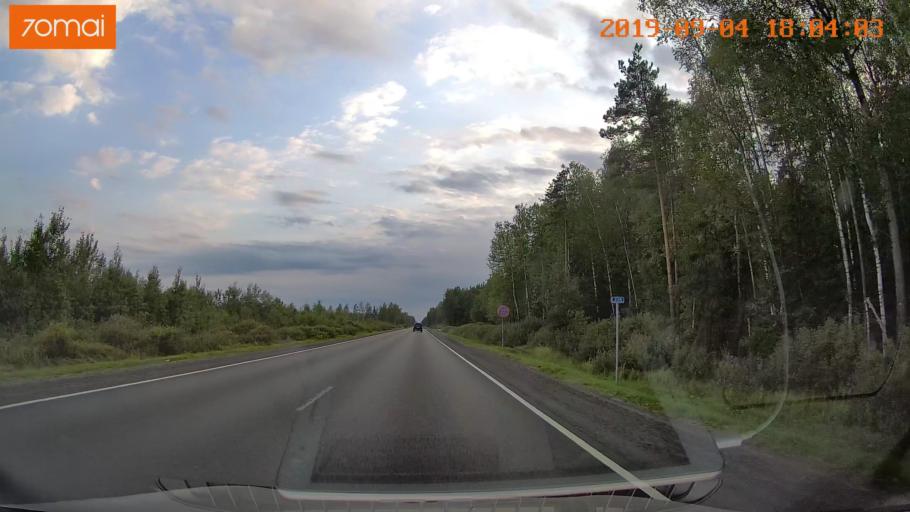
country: RU
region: Moskovskaya
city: Il'inskiy Pogost
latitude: 55.4567
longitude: 38.8442
